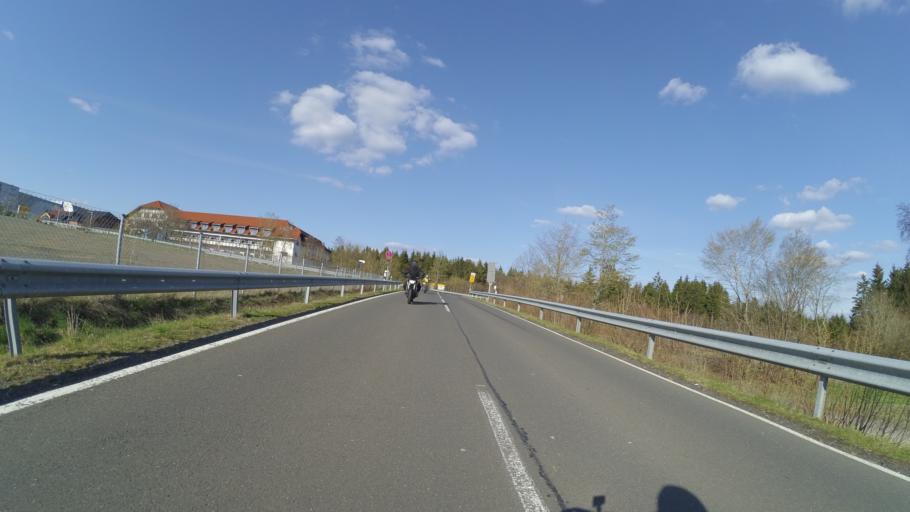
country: DE
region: Rheinland-Pfalz
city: Nurburg
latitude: 50.3297
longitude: 6.9458
